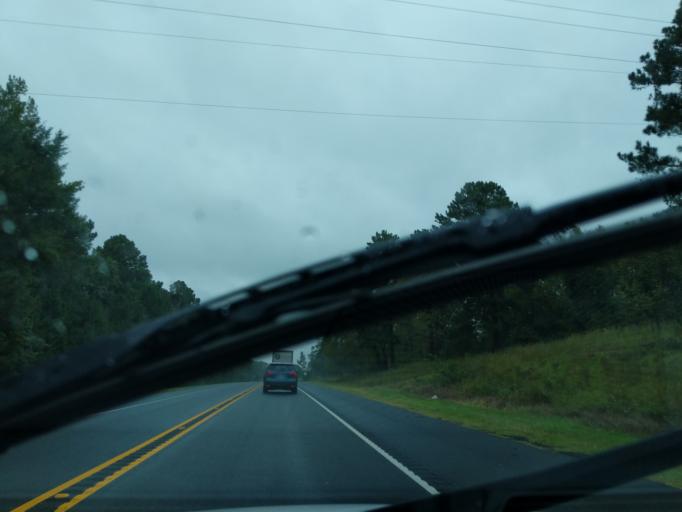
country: US
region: Louisiana
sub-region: Caddo Parish
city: Greenwood
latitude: 32.4301
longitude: -93.9849
